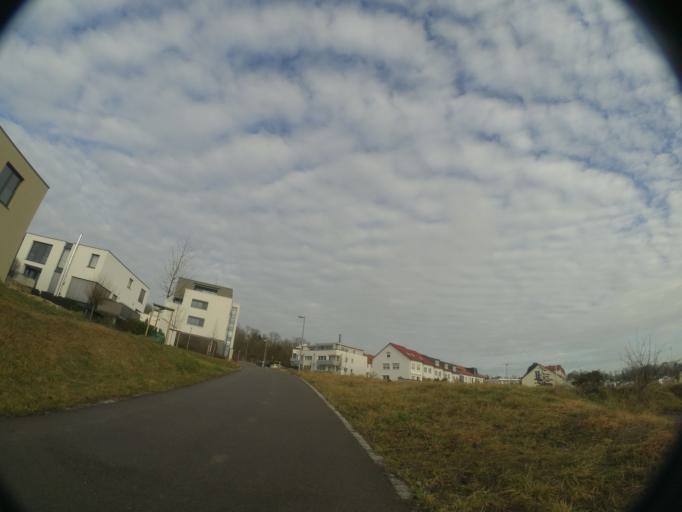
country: DE
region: Baden-Wuerttemberg
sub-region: Tuebingen Region
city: Ulm
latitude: 48.3778
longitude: 9.9499
